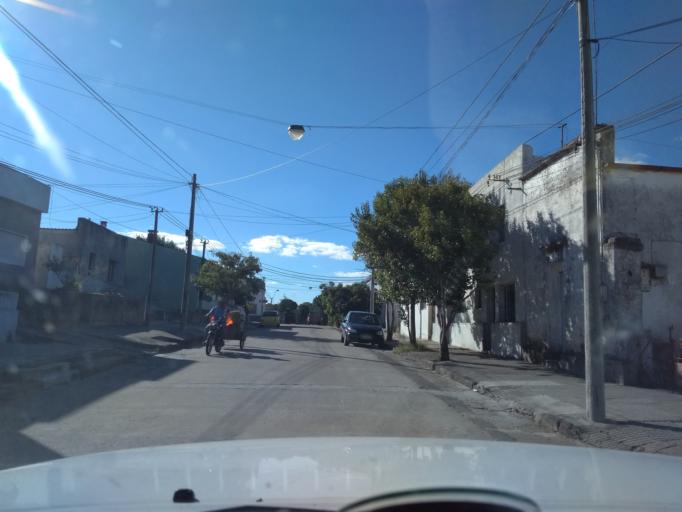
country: UY
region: Florida
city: Florida
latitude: -34.0924
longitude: -56.2136
